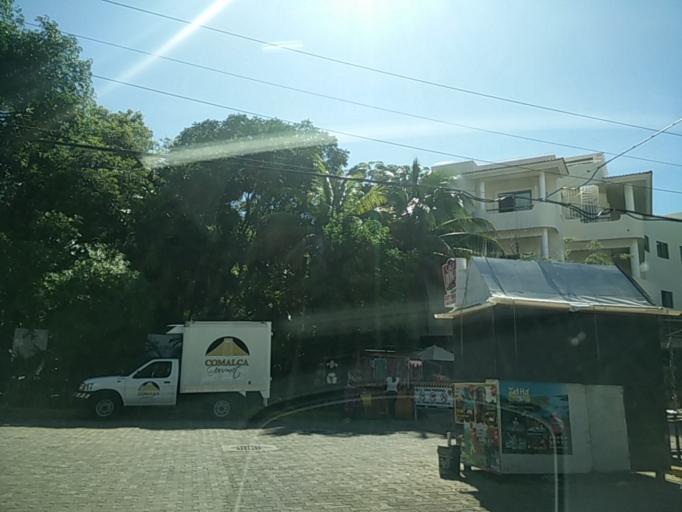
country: MX
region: Quintana Roo
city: Playa del Carmen
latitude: 20.6340
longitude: -87.0674
